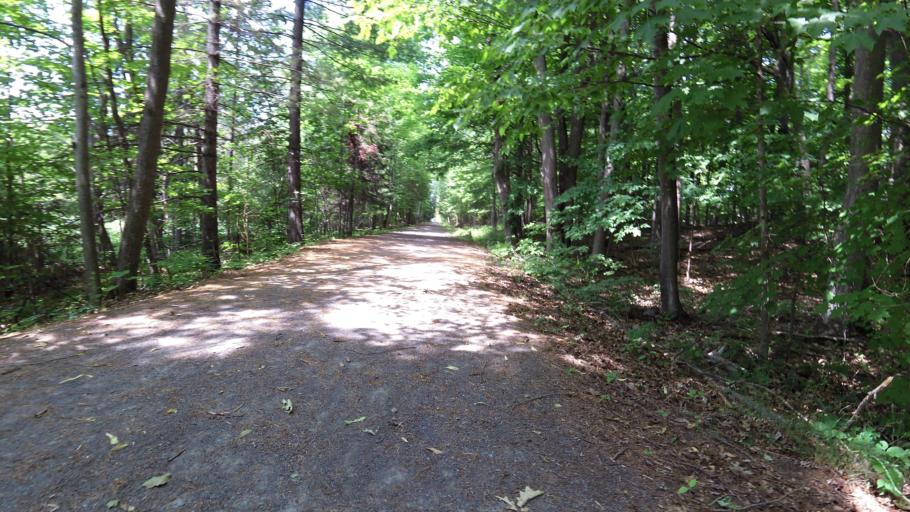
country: CA
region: Ontario
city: Arnprior
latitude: 45.4594
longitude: -76.2681
